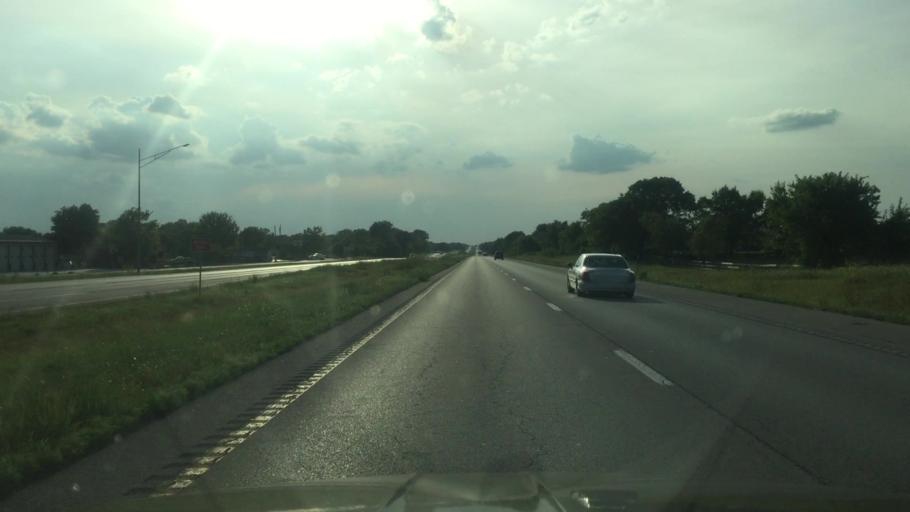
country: US
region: Missouri
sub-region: Jackson County
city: Lone Jack
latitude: 38.8729
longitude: -94.1927
